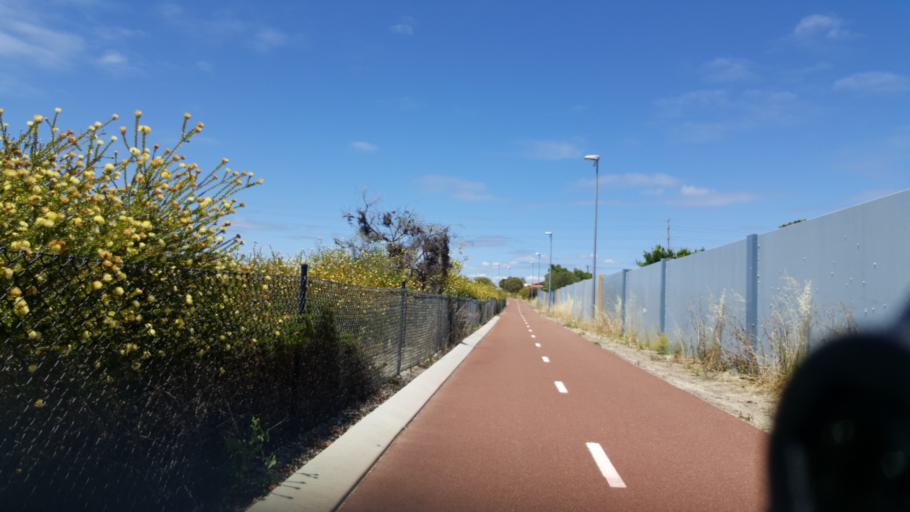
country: AU
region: Western Australia
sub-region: Bayswater
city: Embleton
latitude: -31.8688
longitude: 115.8870
